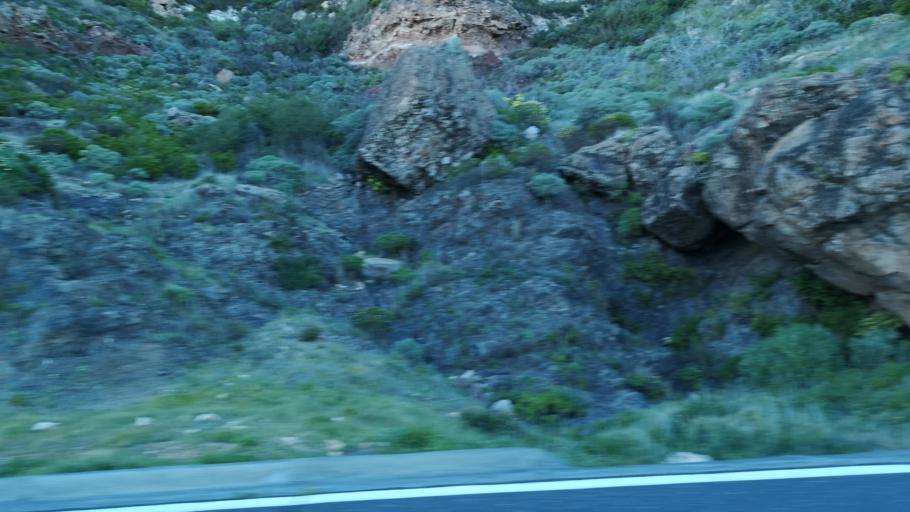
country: ES
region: Canary Islands
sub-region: Provincia de Santa Cruz de Tenerife
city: Alajero
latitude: 28.0864
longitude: -17.2484
